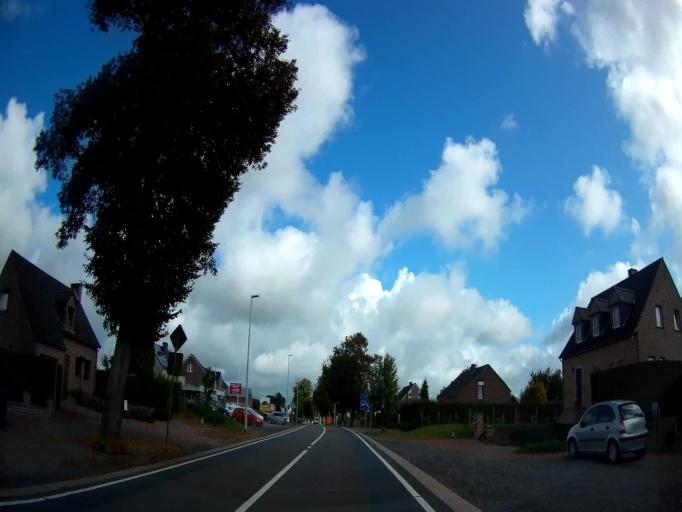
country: BE
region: Wallonia
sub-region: Province de Liege
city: Dison
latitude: 50.6492
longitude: 5.8809
